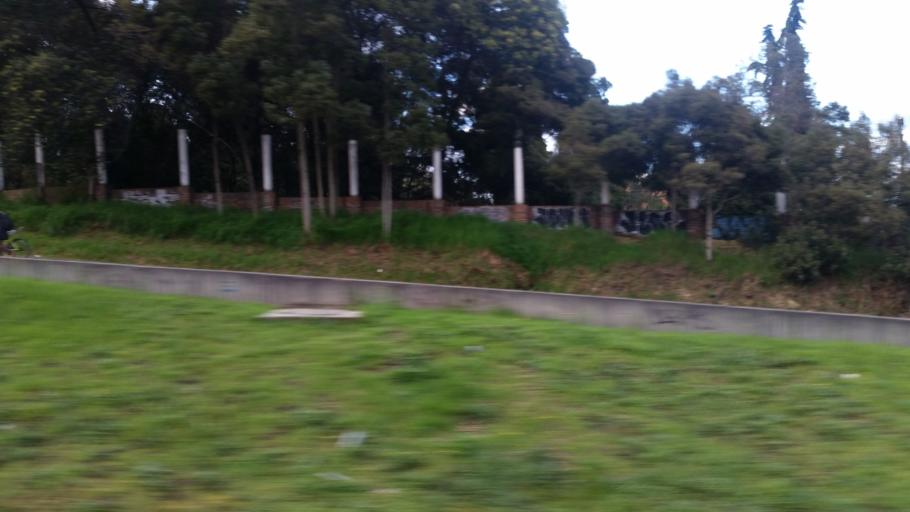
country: CO
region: Cundinamarca
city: Cota
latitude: 4.7333
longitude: -74.0775
